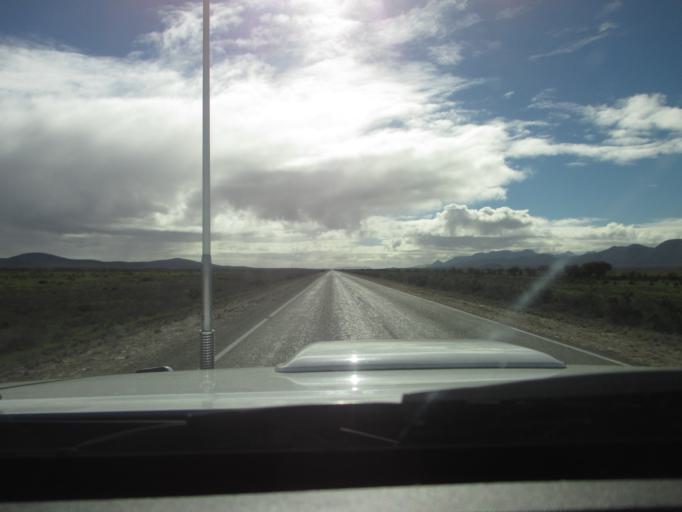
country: AU
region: South Australia
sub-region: Flinders Ranges
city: Quorn
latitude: -31.6851
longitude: 138.3640
